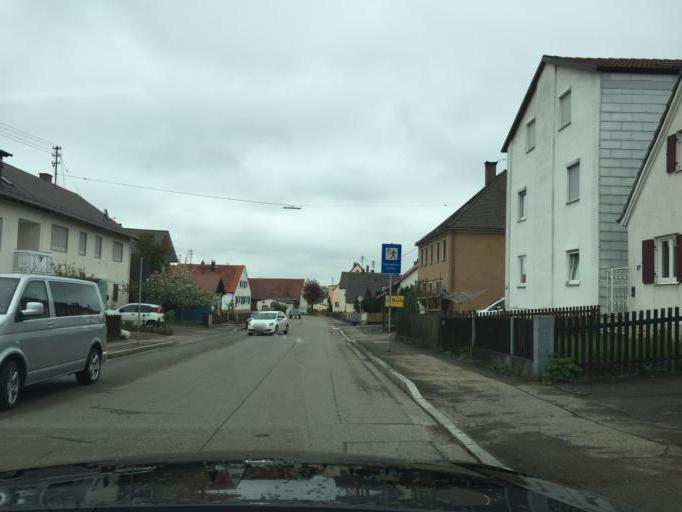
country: DE
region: Bavaria
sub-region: Swabia
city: Wertingen
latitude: 48.5596
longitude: 10.6760
